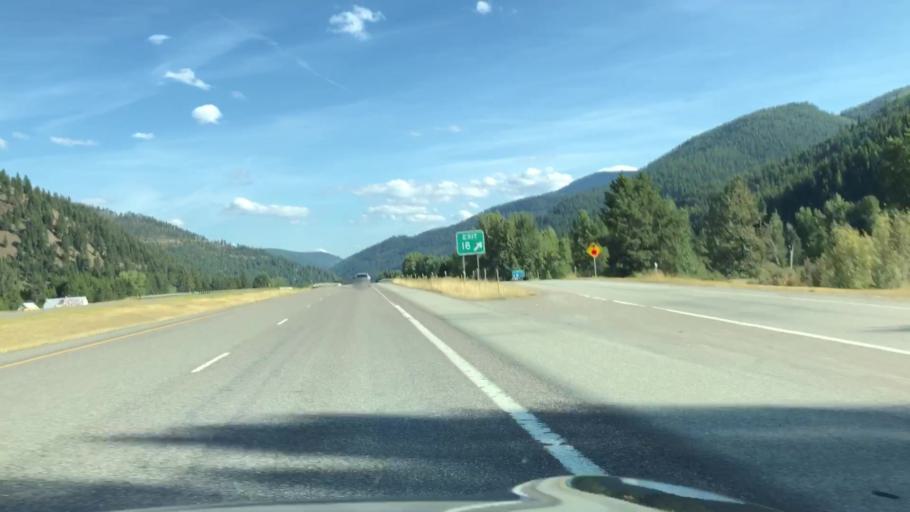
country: US
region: Montana
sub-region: Sanders County
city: Thompson Falls
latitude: 47.3770
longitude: -115.3542
